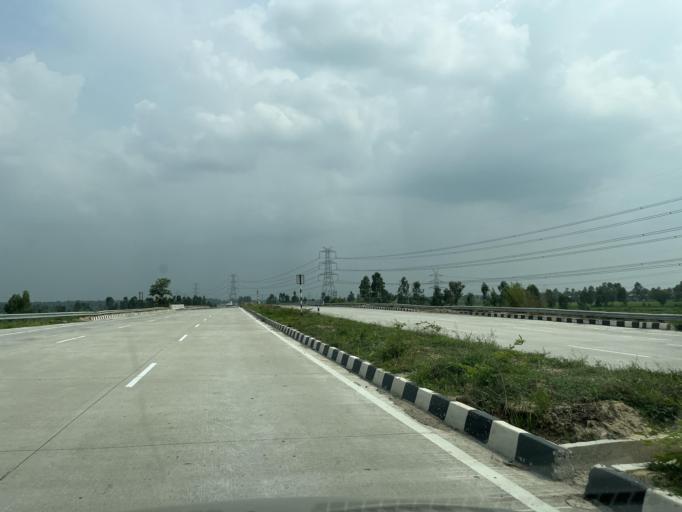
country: IN
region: Uttarakhand
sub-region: Udham Singh Nagar
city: Jaspur
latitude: 29.2891
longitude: 78.8531
